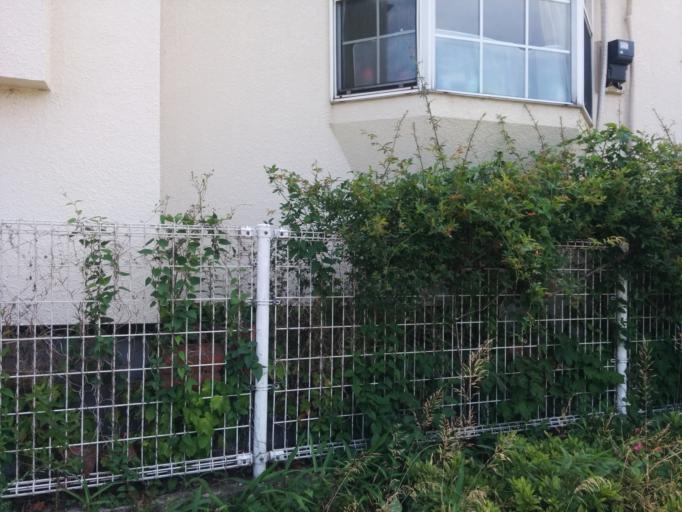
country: JP
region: Tokyo
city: Higashimurayama-shi
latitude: 35.7630
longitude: 139.4839
